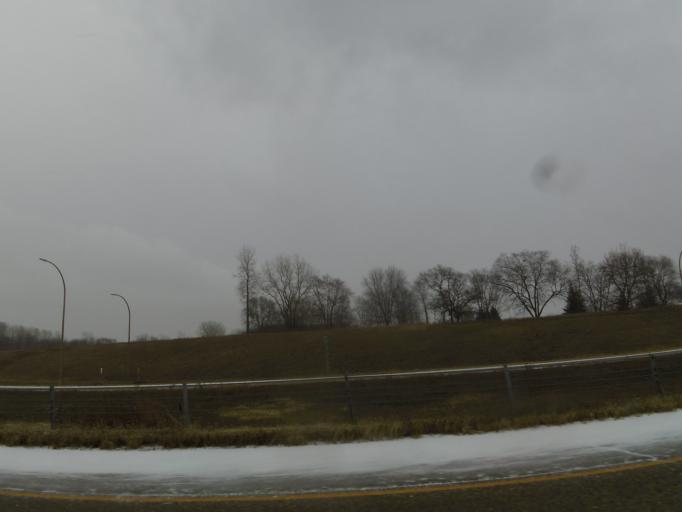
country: US
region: Minnesota
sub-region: Dakota County
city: Eagan
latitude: 44.8022
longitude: -93.2220
